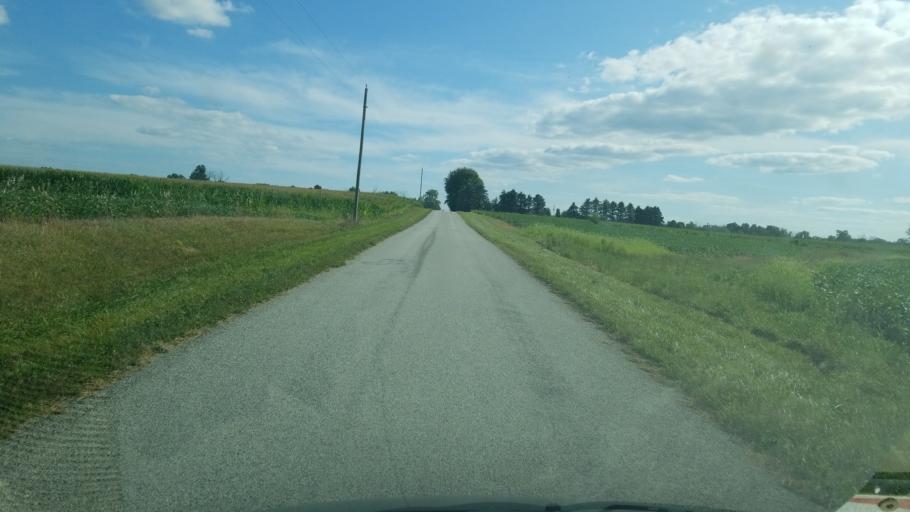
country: US
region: Ohio
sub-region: Champaign County
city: Saint Paris
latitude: 40.1432
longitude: -83.8723
